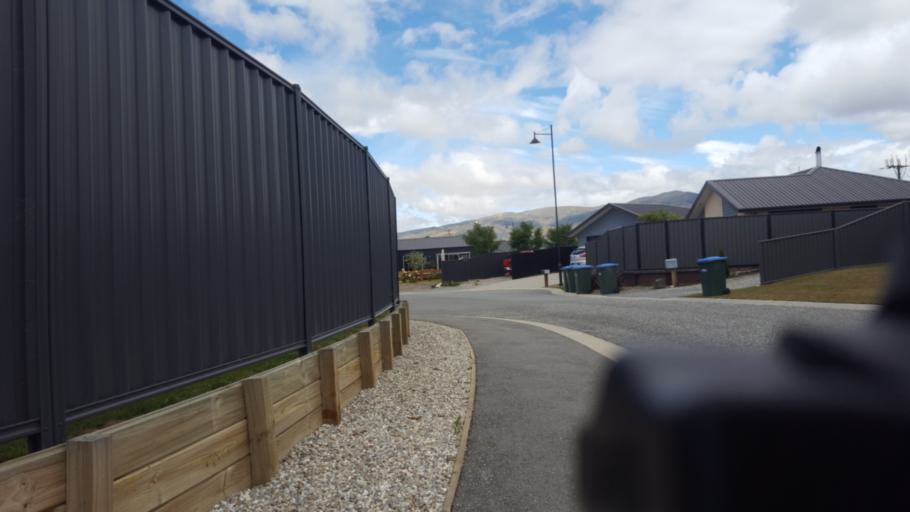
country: NZ
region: Otago
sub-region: Queenstown-Lakes District
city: Wanaka
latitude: -45.0460
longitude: 169.1789
